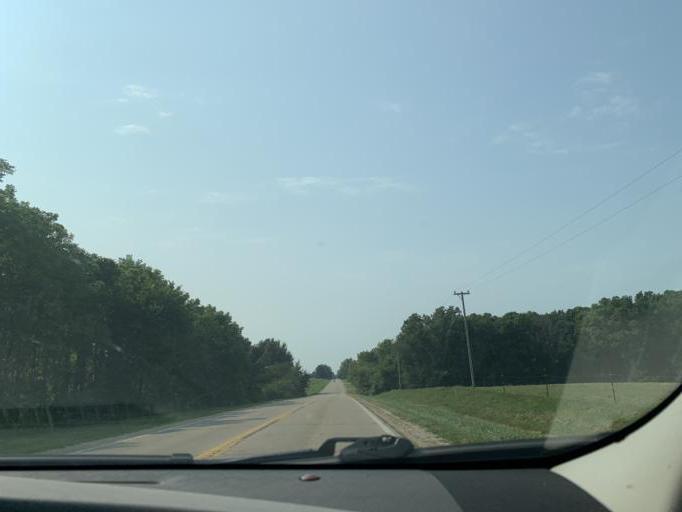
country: US
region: Illinois
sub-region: Whiteside County
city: Sterling
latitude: 41.8173
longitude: -89.7421
